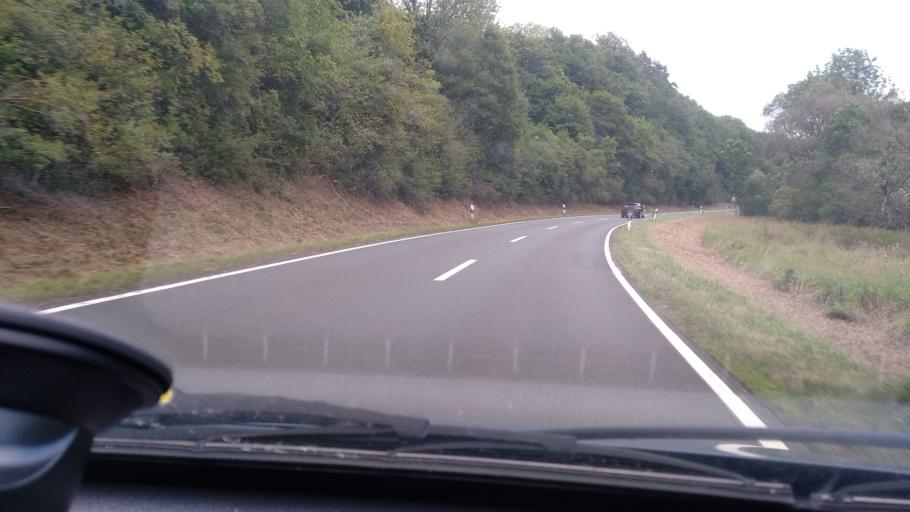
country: DE
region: Hesse
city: Dillenburg
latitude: 50.7777
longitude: 8.3426
